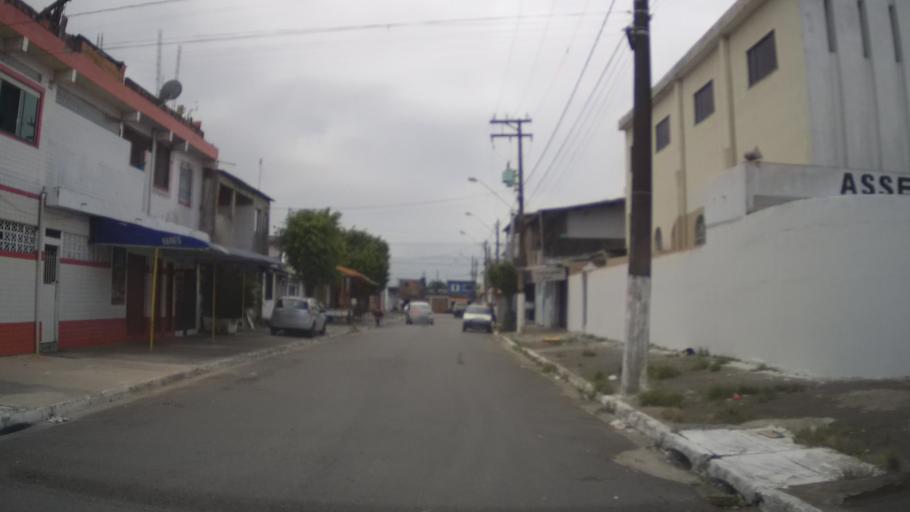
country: BR
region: Sao Paulo
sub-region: Praia Grande
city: Praia Grande
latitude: -24.0193
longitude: -46.4843
